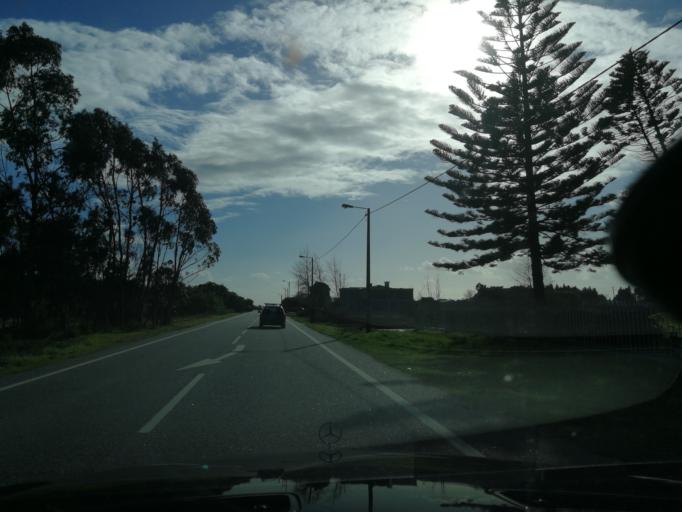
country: PT
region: Aveiro
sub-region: Estarreja
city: Pardilho
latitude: 40.7945
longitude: -8.6738
